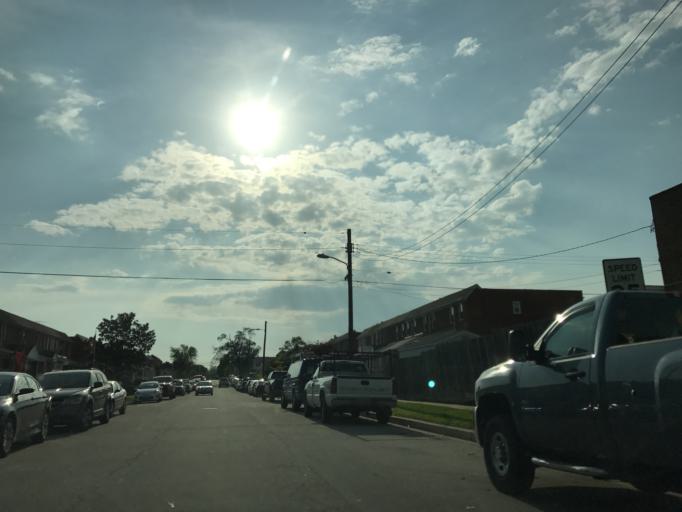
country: US
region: Maryland
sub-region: Baltimore County
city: Middle River
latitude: 39.3373
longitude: -76.4423
